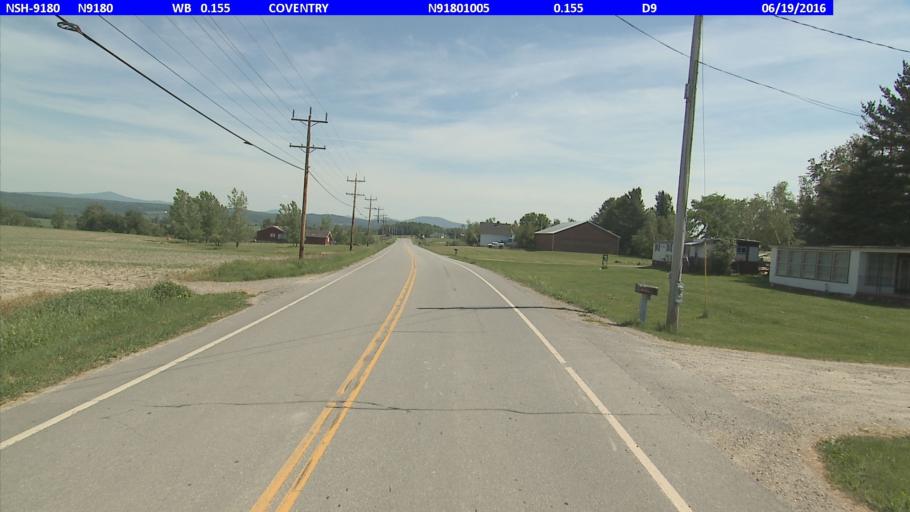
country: US
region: Vermont
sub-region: Orleans County
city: Newport
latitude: 44.8911
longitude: -72.2246
